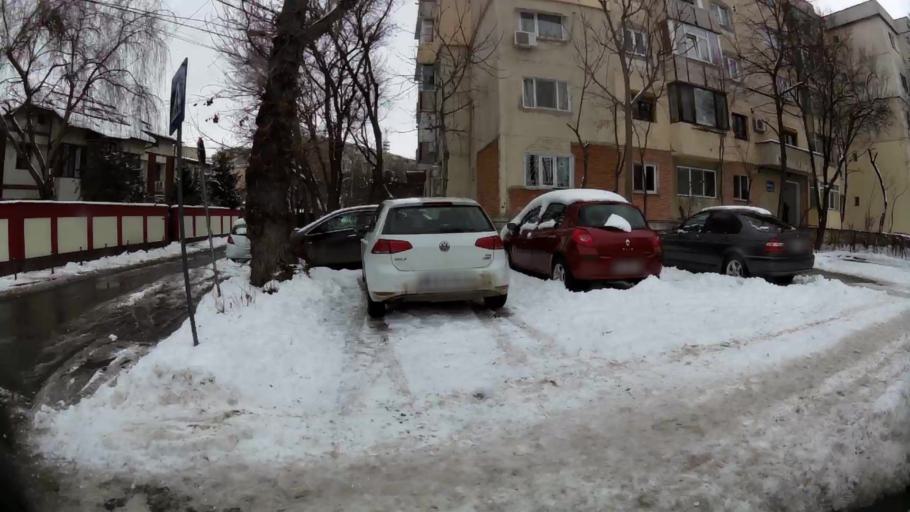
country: RO
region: Bucuresti
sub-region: Municipiul Bucuresti
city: Bucuresti
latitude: 44.3941
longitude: 26.1151
